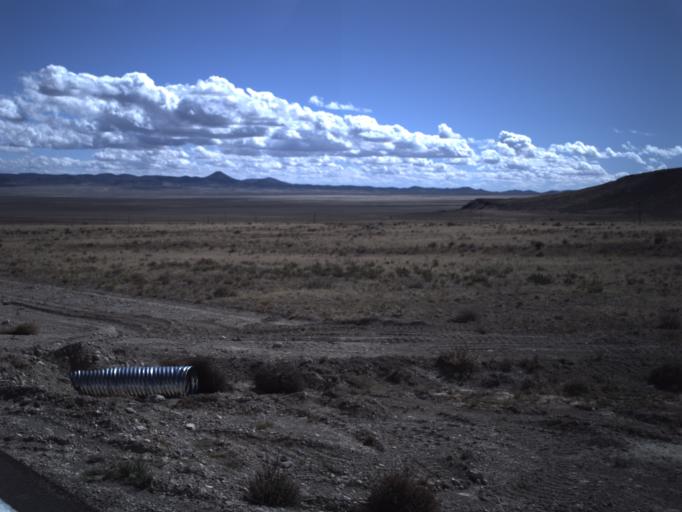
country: US
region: Utah
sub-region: Beaver County
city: Milford
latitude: 38.4907
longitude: -113.4691
